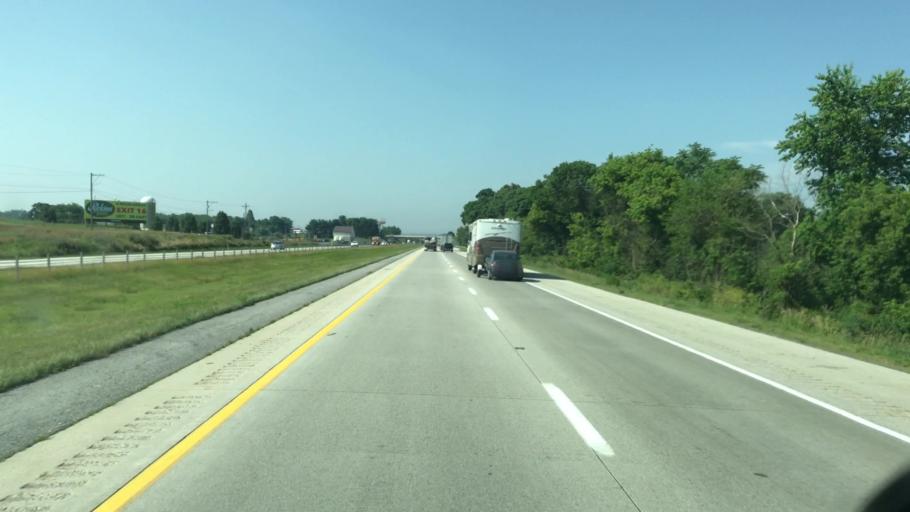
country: US
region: Pennsylvania
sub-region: Franklin County
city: Scotland
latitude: 39.9707
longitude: -77.5745
